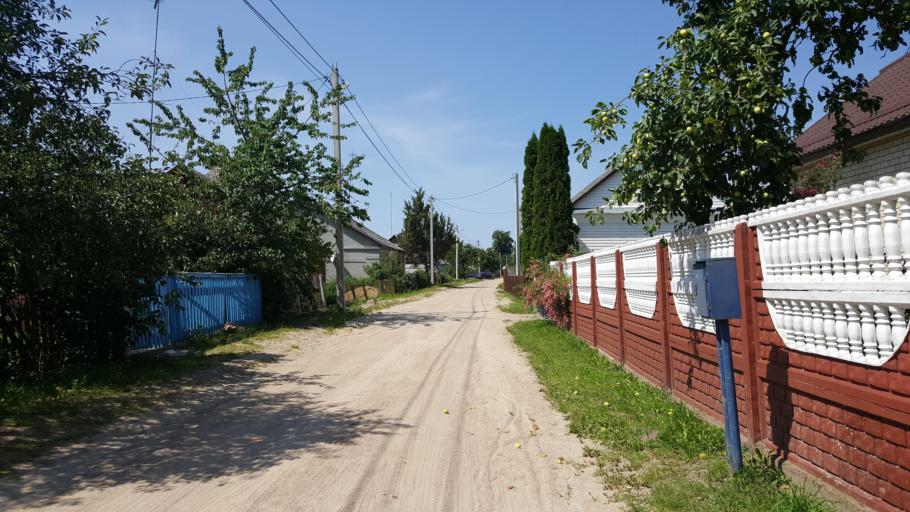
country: BY
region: Brest
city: Vysokaye
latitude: 52.3644
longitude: 23.3784
